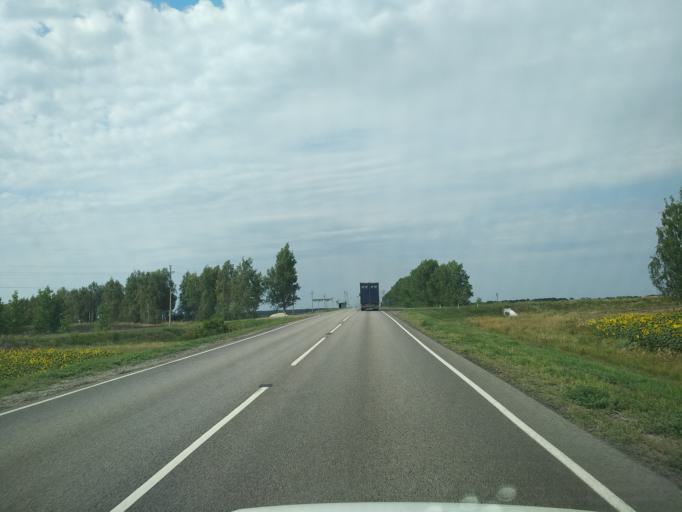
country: RU
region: Voronezj
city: Pereleshinskiy
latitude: 51.8419
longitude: 40.3041
